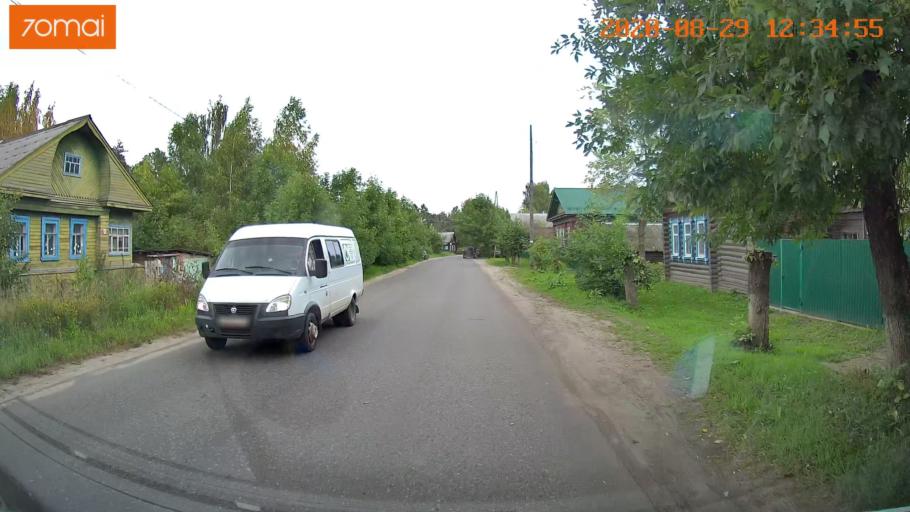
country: RU
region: Ivanovo
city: Yur'yevets
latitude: 57.3118
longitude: 43.1033
